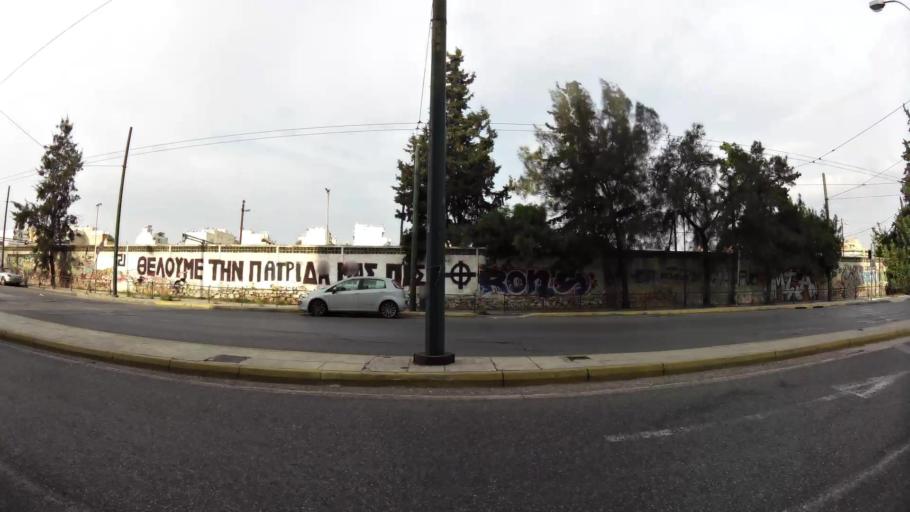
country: GR
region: Attica
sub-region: Nomarchia Athinas
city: Athens
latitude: 37.9908
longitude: 23.7206
